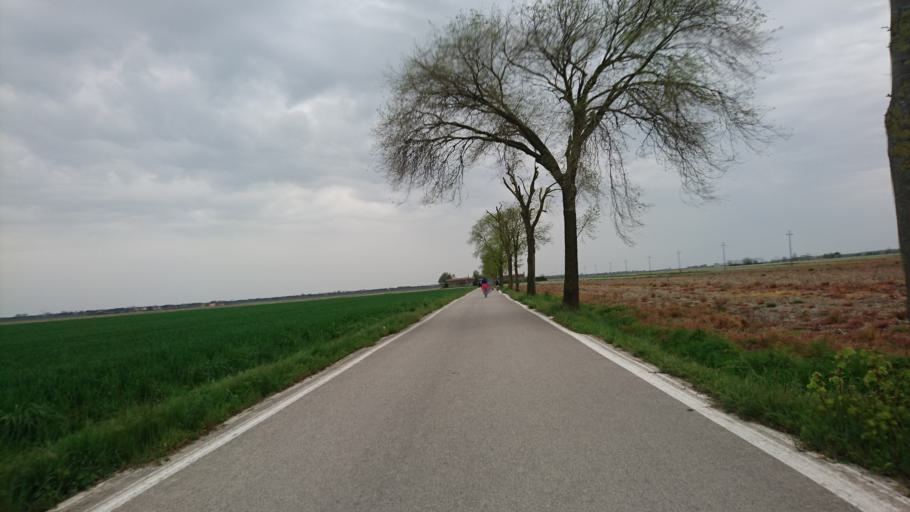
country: IT
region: Veneto
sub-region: Provincia di Venezia
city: Bibione
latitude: 45.6595
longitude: 13.0018
